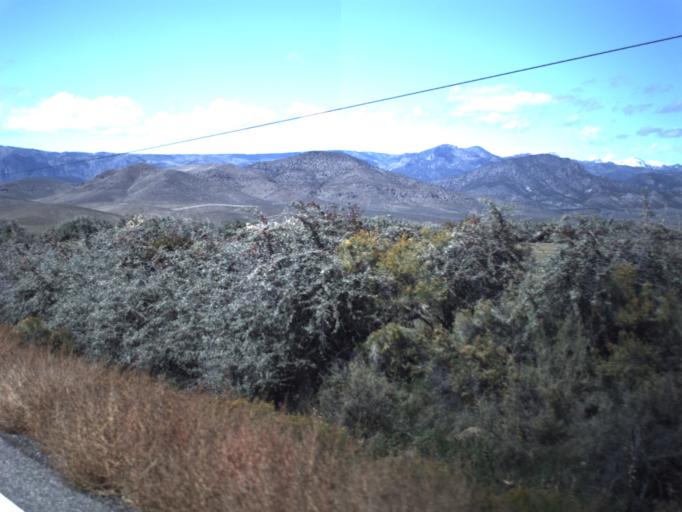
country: US
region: Utah
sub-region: Piute County
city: Junction
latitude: 38.2084
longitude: -112.2043
